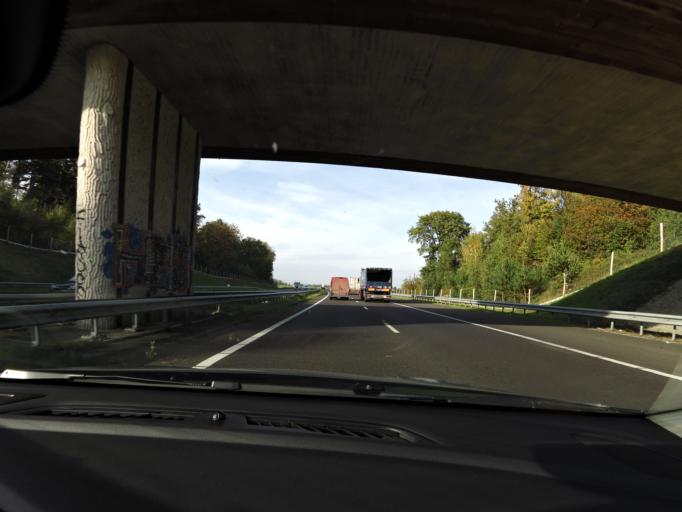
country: NL
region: North Brabant
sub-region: Gemeente Bergen op Zoom
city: Bergen op Zoom
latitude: 51.5264
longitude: 4.3097
